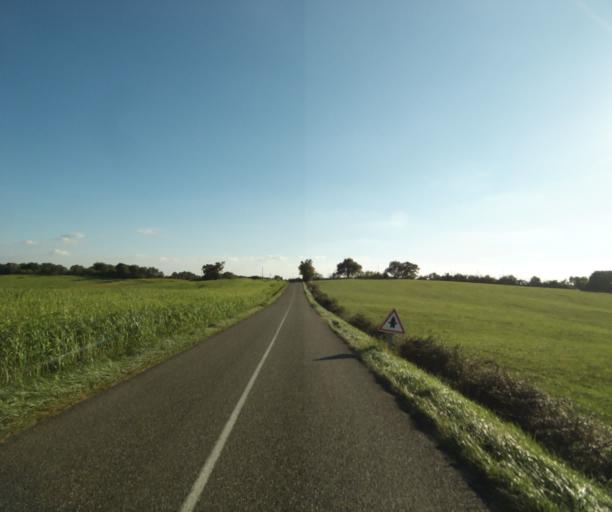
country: FR
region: Midi-Pyrenees
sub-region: Departement du Gers
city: Eauze
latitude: 43.7652
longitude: 0.1285
